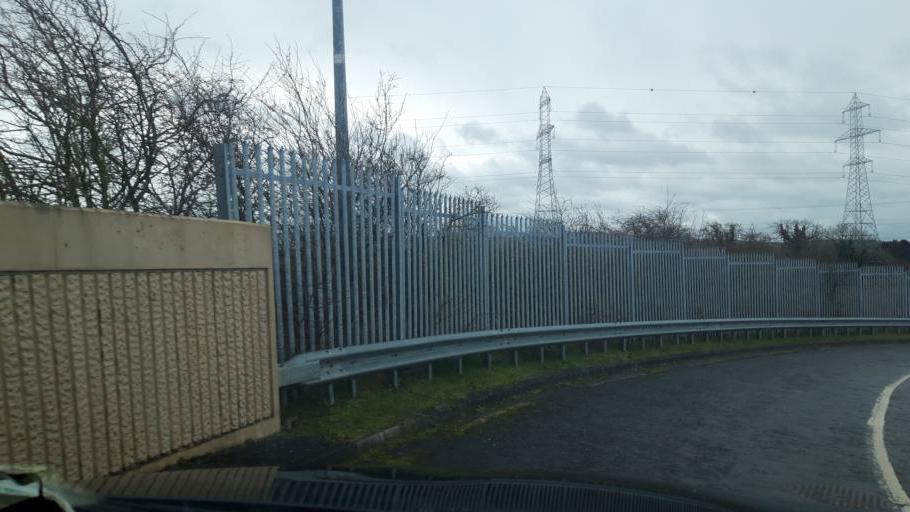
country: IE
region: Leinster
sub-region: South Dublin
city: Newcastle
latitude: 53.3331
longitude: -6.5011
